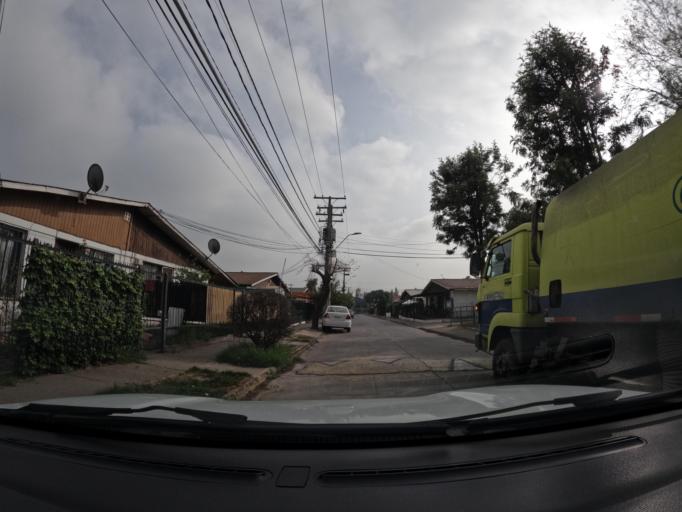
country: CL
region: Santiago Metropolitan
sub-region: Provincia de Santiago
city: Villa Presidente Frei, Nunoa, Santiago, Chile
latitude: -33.4714
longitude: -70.5497
